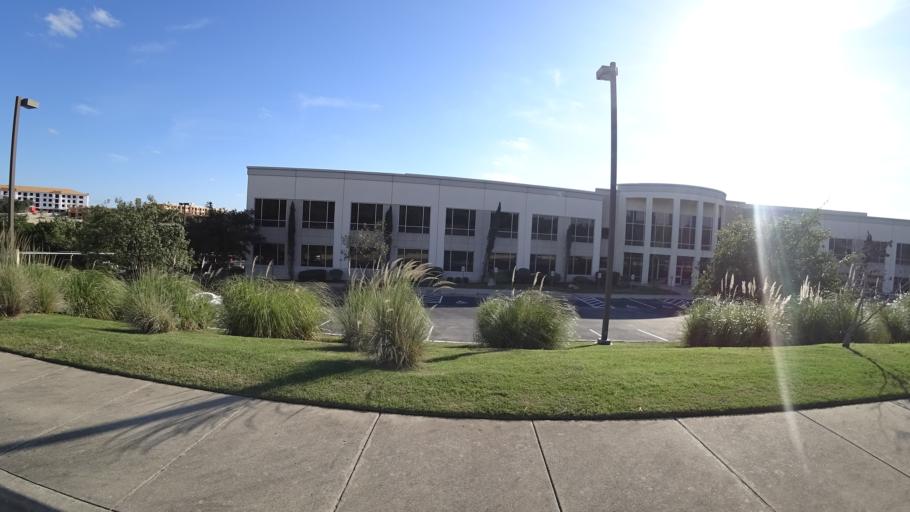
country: US
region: Texas
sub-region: Travis County
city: Barton Creek
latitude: 30.2496
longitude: -97.8646
